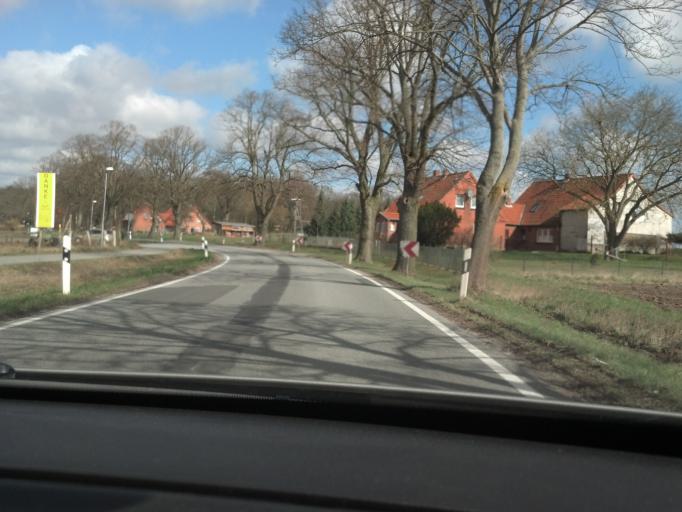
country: DE
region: Mecklenburg-Vorpommern
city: Boizenburg
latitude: 53.4014
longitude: 10.7498
